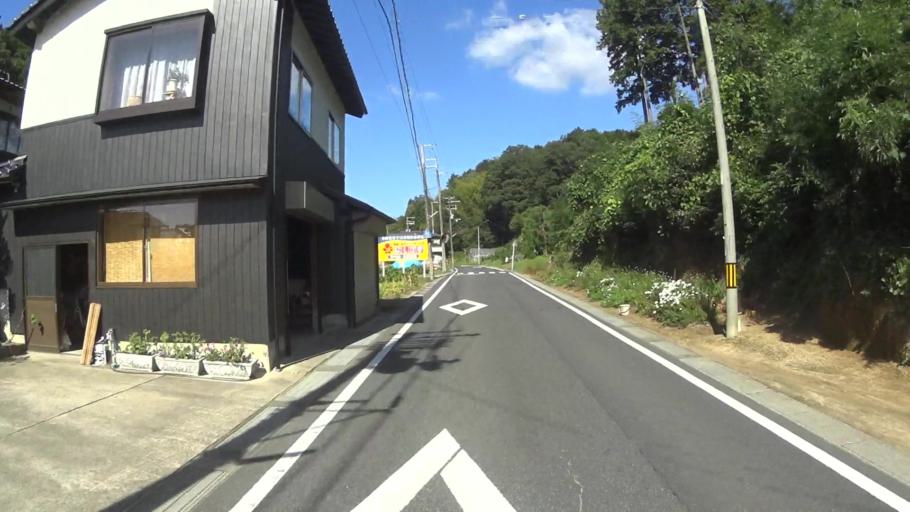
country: JP
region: Kyoto
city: Miyazu
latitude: 35.6333
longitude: 135.0725
